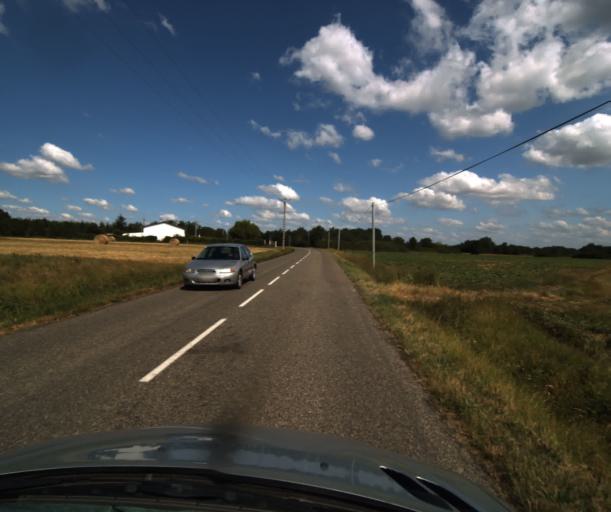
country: FR
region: Midi-Pyrenees
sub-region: Departement du Tarn-et-Garonne
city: Campsas
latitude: 43.9065
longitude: 1.2907
